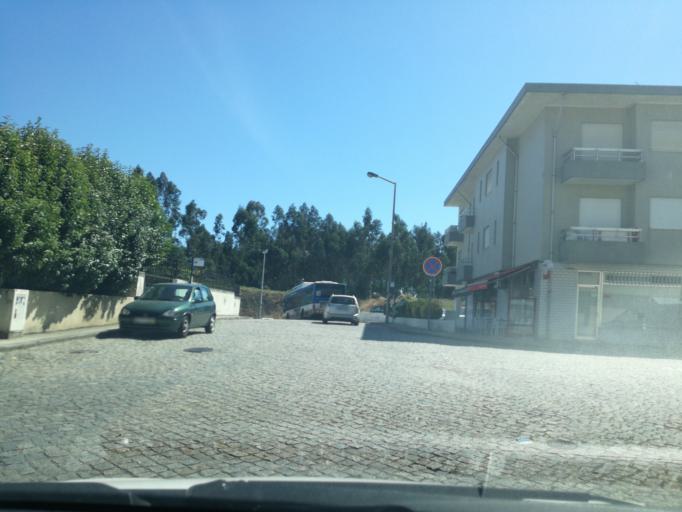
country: PT
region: Porto
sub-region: Maia
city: Maia
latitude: 41.2372
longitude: -8.6126
